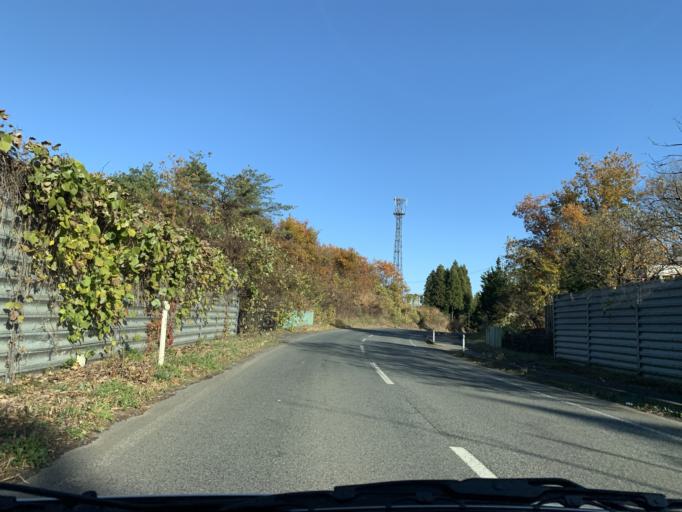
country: JP
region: Iwate
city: Kitakami
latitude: 39.2375
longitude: 141.0811
